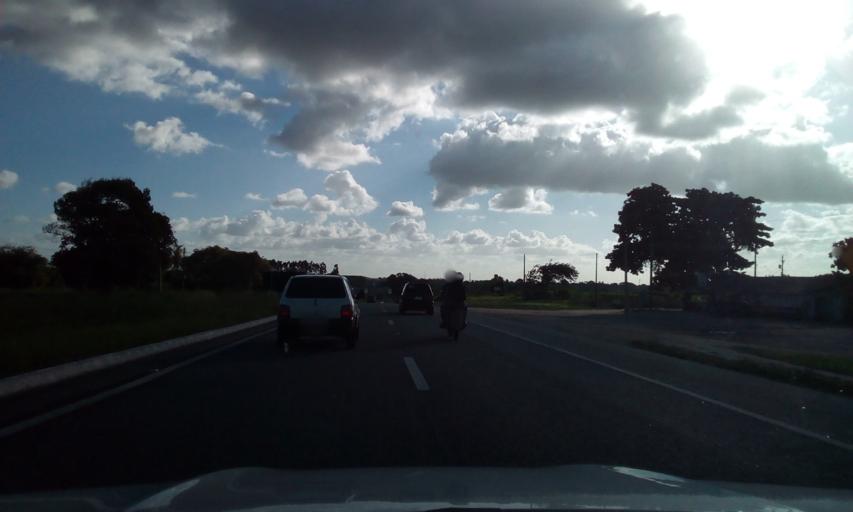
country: BR
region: Paraiba
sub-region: Cruz Do Espirito Santo
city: Cruz do Espirito Santo
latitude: -7.2034
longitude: -35.1196
